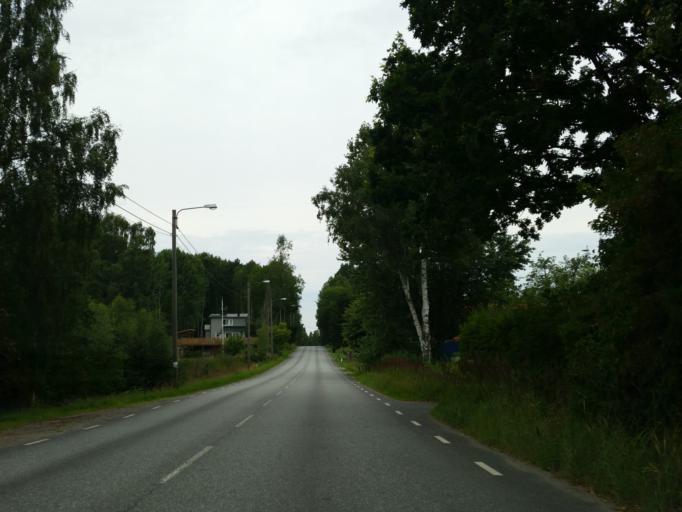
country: SE
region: Stockholm
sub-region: Sodertalje Kommun
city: Soedertaelje
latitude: 59.1986
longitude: 17.5803
